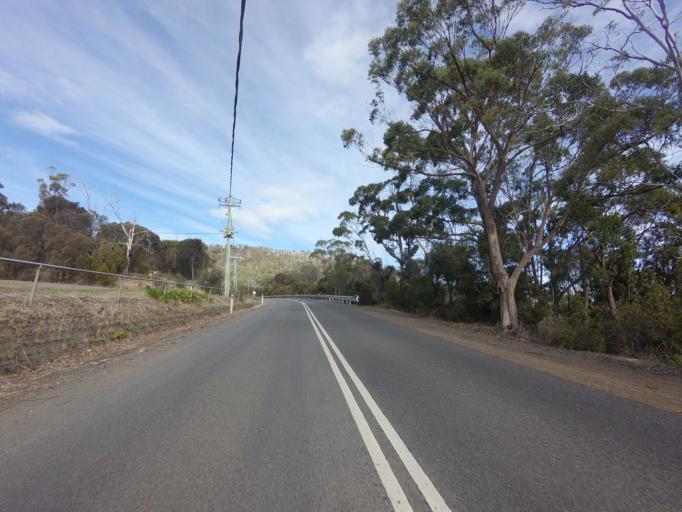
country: AU
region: Tasmania
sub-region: Clarence
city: Sandford
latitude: -43.1086
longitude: 147.7458
